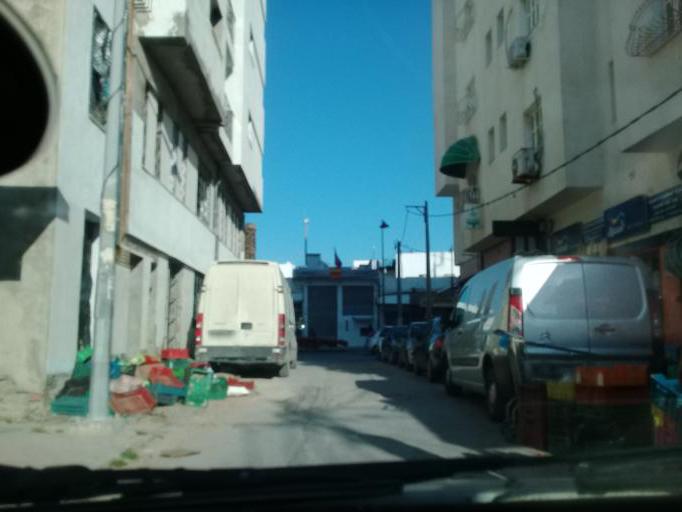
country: TN
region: Tunis
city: La Goulette
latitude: 36.8188
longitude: 10.3056
